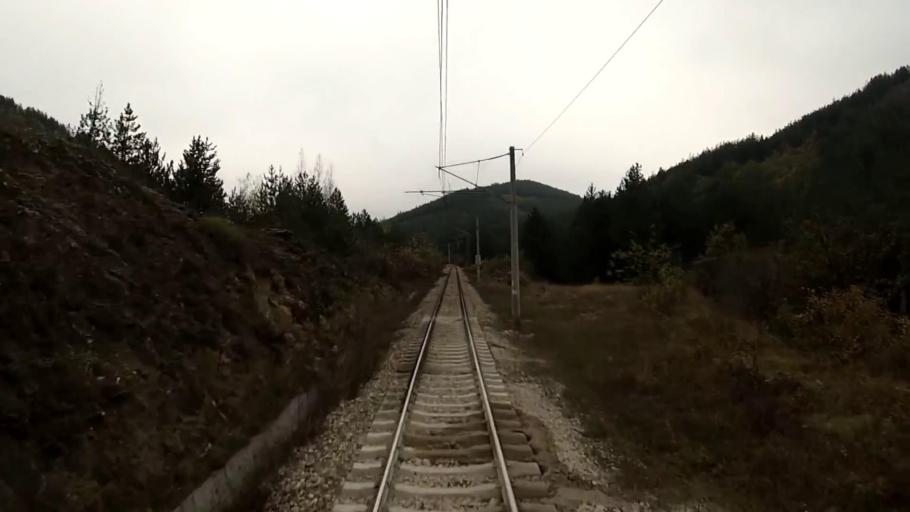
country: BG
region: Sofiya
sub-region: Obshtina Dragoman
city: Dragoman
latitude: 42.9483
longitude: 22.9019
